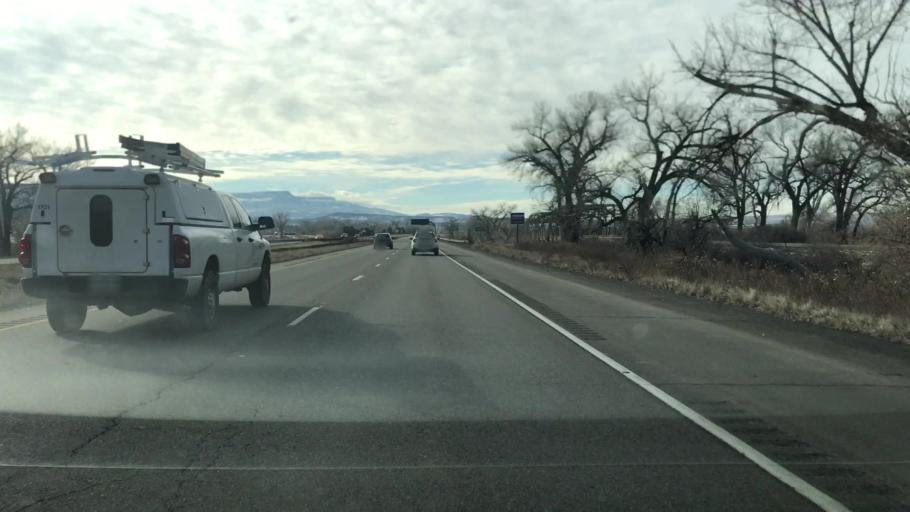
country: US
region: Colorado
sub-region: Garfield County
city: Parachute
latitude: 39.3406
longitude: -108.1926
